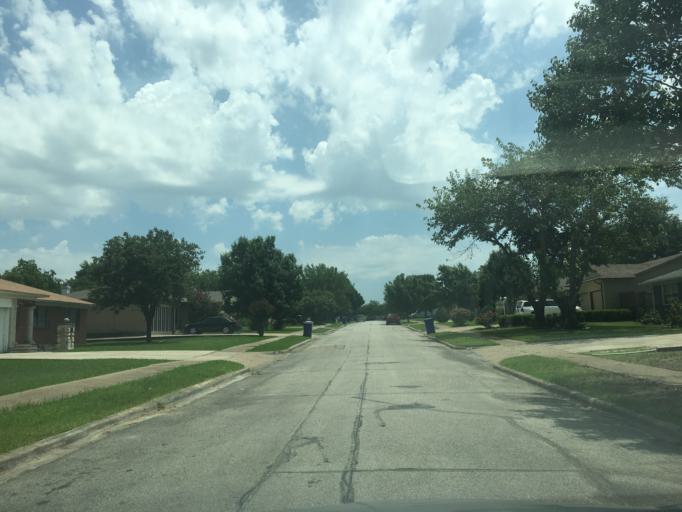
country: US
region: Texas
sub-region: Dallas County
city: Carrollton
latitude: 32.9414
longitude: -96.8763
